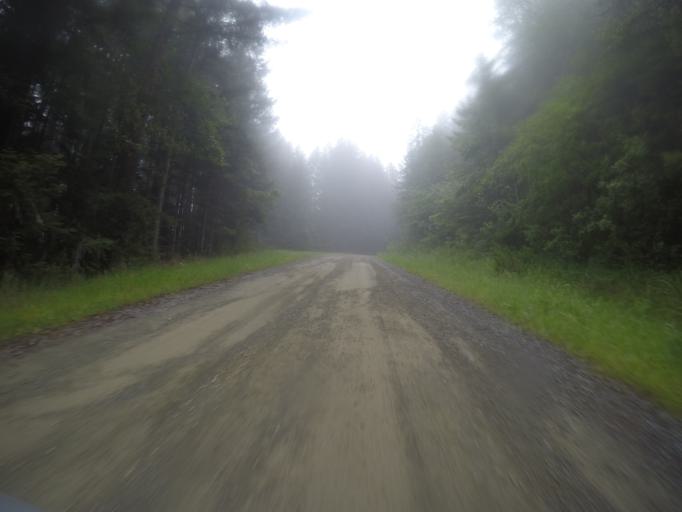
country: US
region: California
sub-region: Humboldt County
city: Westhaven-Moonstone
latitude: 41.2382
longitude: -123.9953
